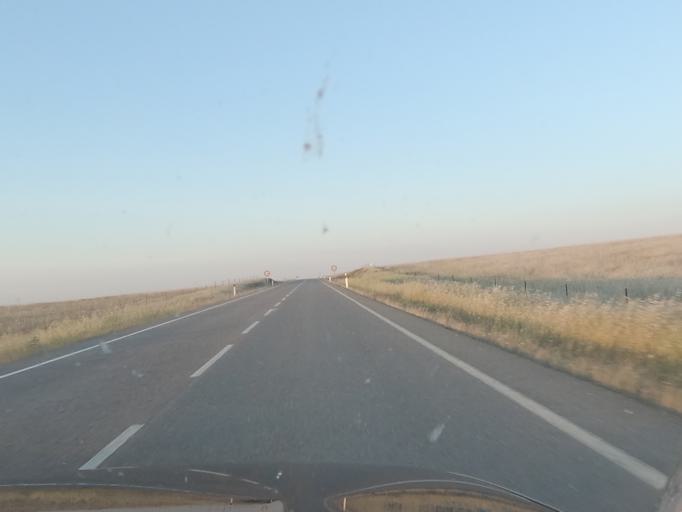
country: ES
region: Extremadura
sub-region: Provincia de Caceres
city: Alcantara
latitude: 39.6297
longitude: -6.9256
